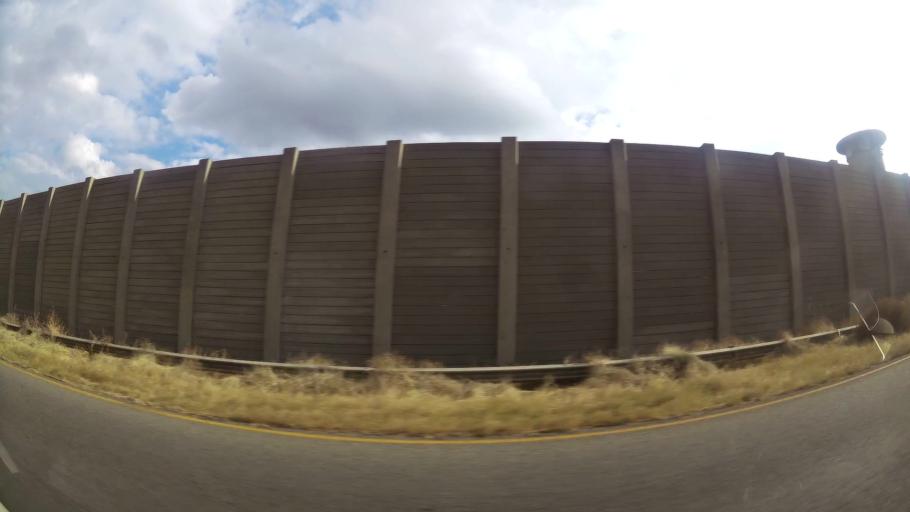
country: ZA
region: Orange Free State
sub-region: Fezile Dabi District Municipality
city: Sasolburg
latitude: -26.8253
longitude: 27.8477
